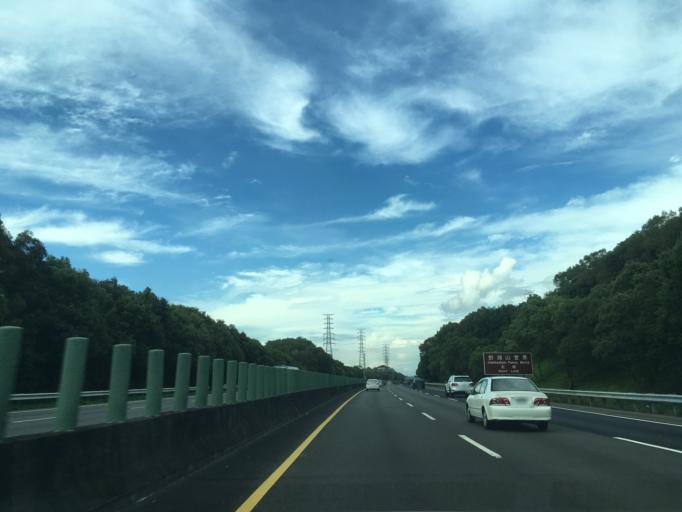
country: TW
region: Taiwan
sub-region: Chiayi
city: Jiayi Shi
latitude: 23.5812
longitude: 120.5112
